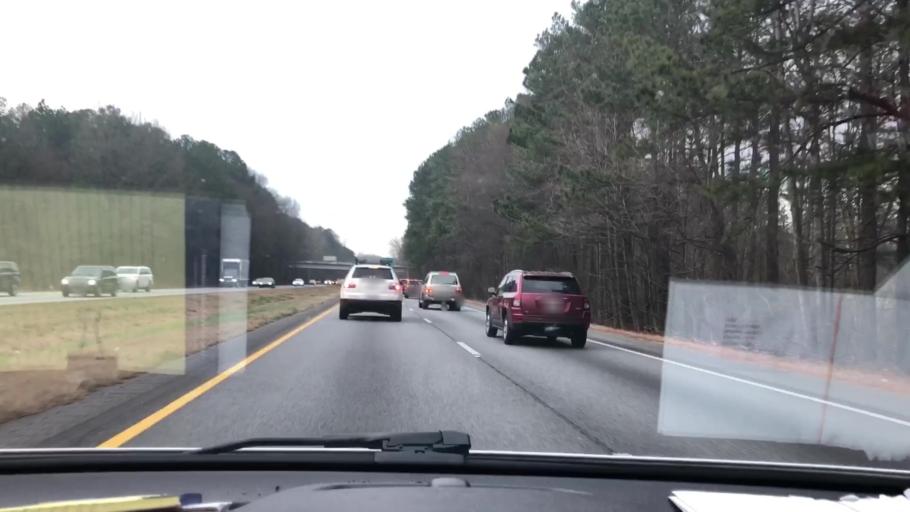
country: US
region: Georgia
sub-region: Gwinnett County
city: Lawrenceville
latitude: 33.9607
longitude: -84.0323
